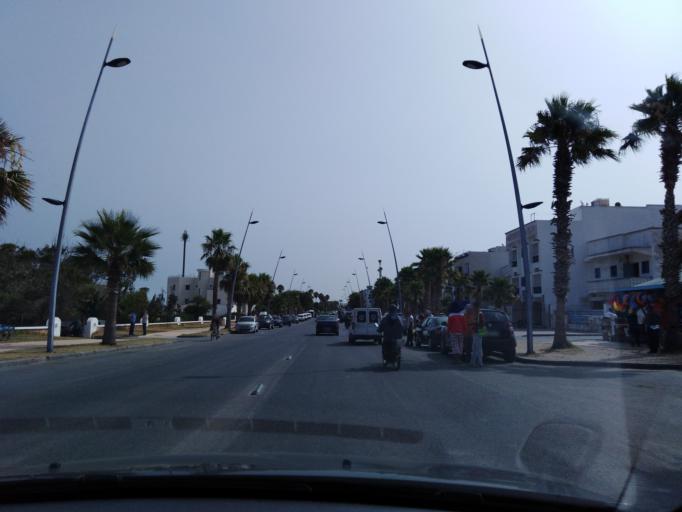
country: MA
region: Doukkala-Abda
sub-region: Safi
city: Safi
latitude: 32.7326
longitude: -9.0351
